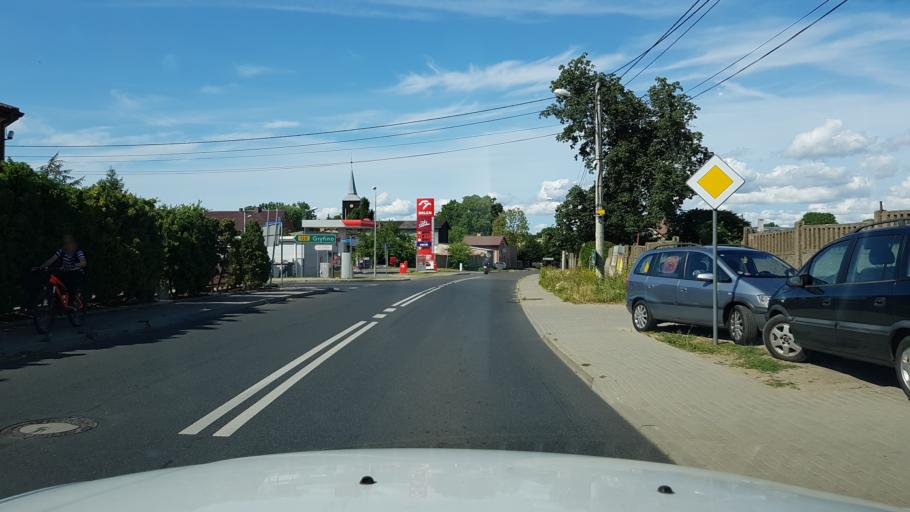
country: PL
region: West Pomeranian Voivodeship
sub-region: Powiat gryfinski
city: Stare Czarnowo
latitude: 53.2782
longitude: 14.7789
